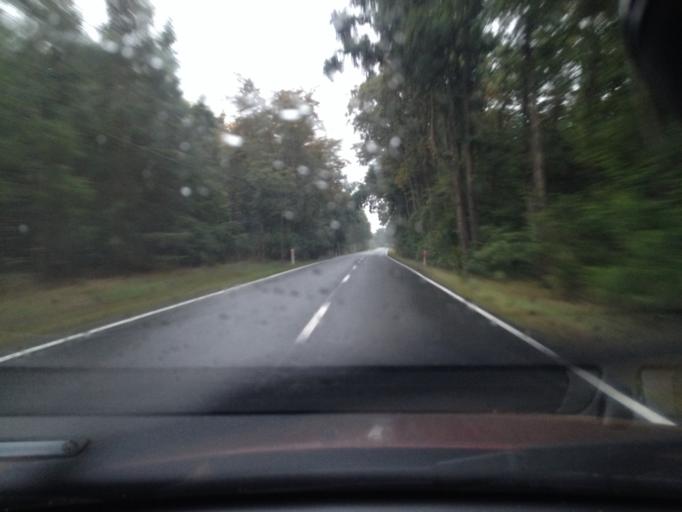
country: PL
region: Lubusz
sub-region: Powiat zaganski
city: Ilowa
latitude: 51.4185
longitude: 15.1900
